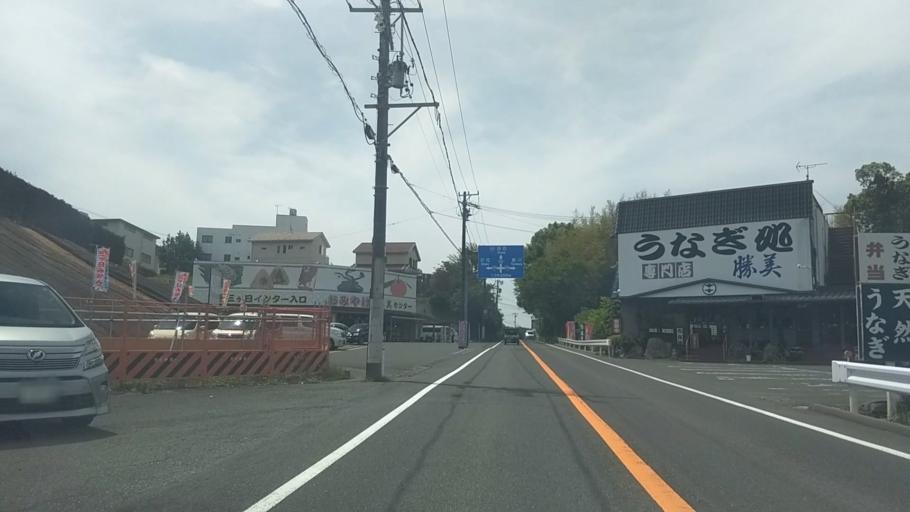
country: JP
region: Shizuoka
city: Kosai-shi
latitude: 34.7959
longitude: 137.5847
